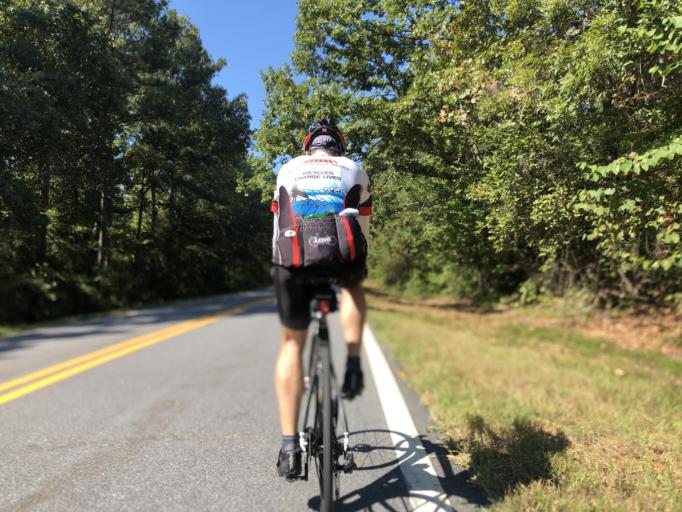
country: US
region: Georgia
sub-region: Coweta County
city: Newnan
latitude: 33.3934
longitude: -84.9648
